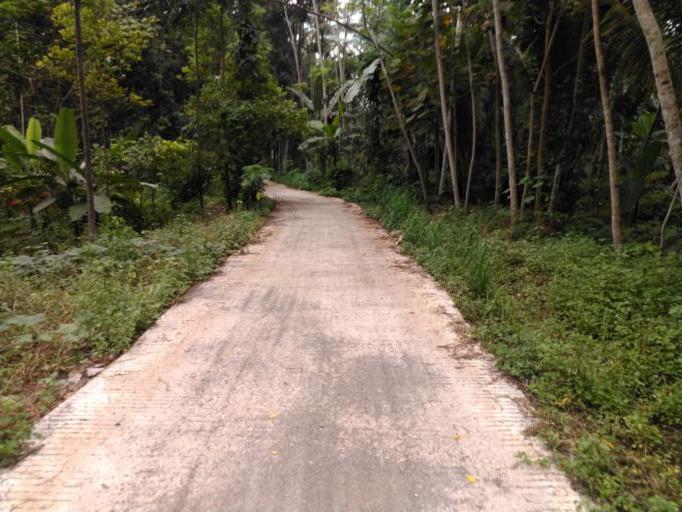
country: ID
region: West Java
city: Cigugur
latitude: -7.6445
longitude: 108.4218
